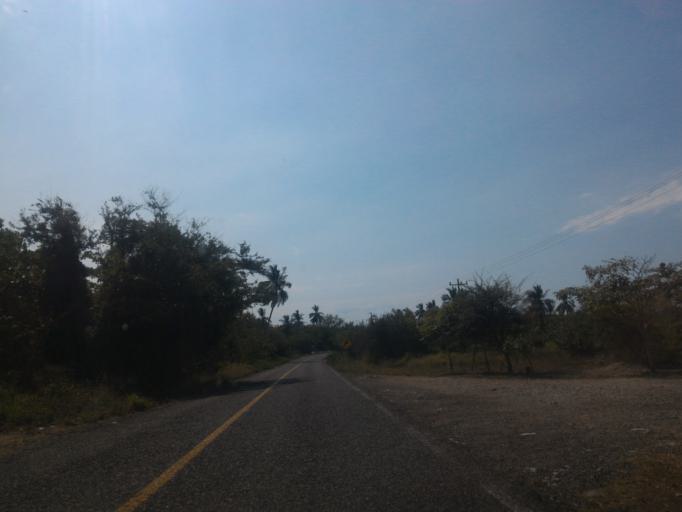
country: MX
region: Michoacan
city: Coahuayana Viejo
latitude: 18.4052
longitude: -103.5281
